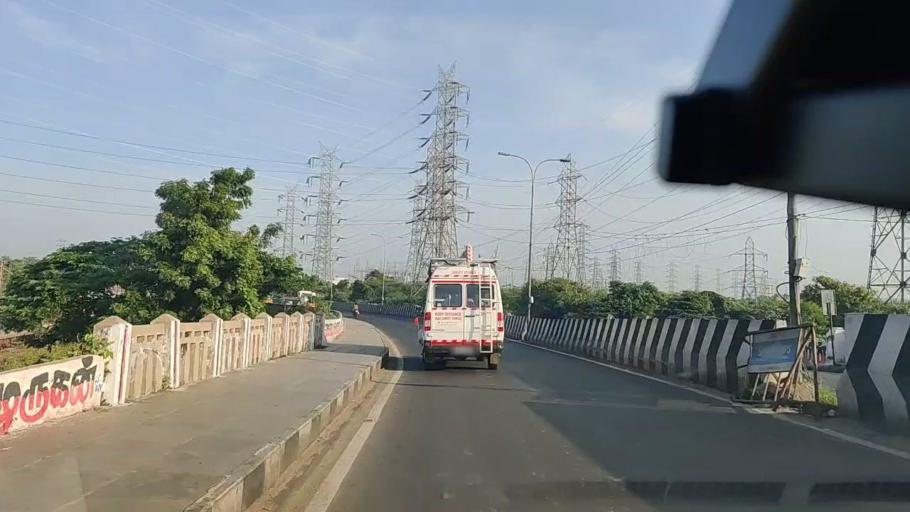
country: IN
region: Tamil Nadu
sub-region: Chennai
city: George Town
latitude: 13.1050
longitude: 80.2711
